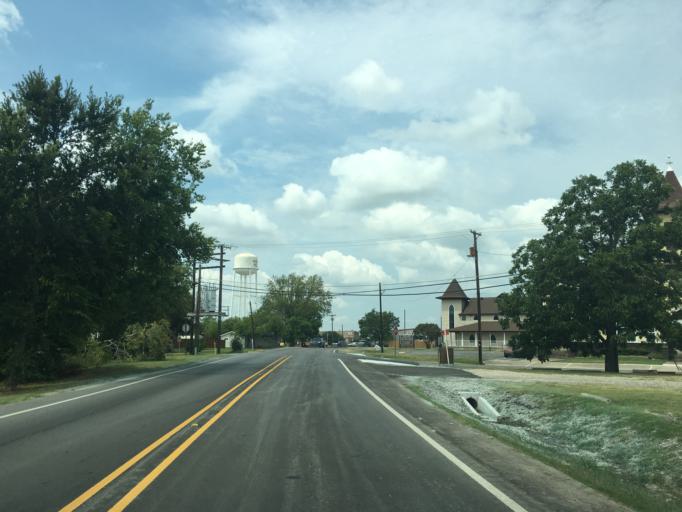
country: US
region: Texas
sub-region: Rockwall County
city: Royse City
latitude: 32.9768
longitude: -96.3279
